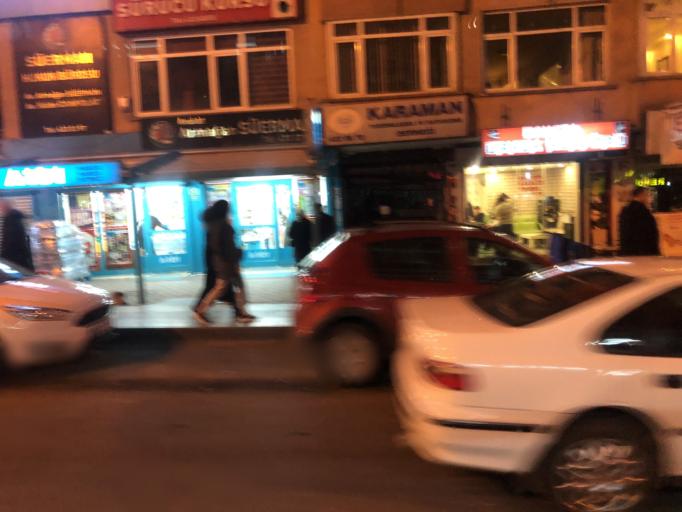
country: TR
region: Ankara
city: Cankaya
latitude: 39.9197
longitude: 32.8591
